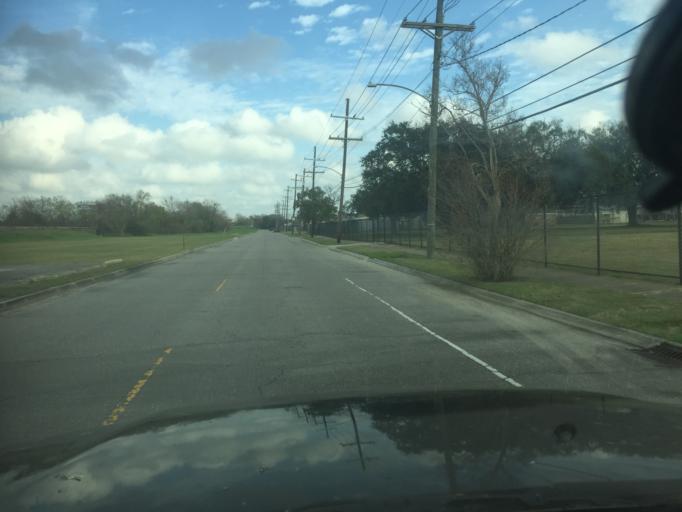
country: US
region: Louisiana
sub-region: Orleans Parish
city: New Orleans
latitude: 29.9919
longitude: -90.0818
